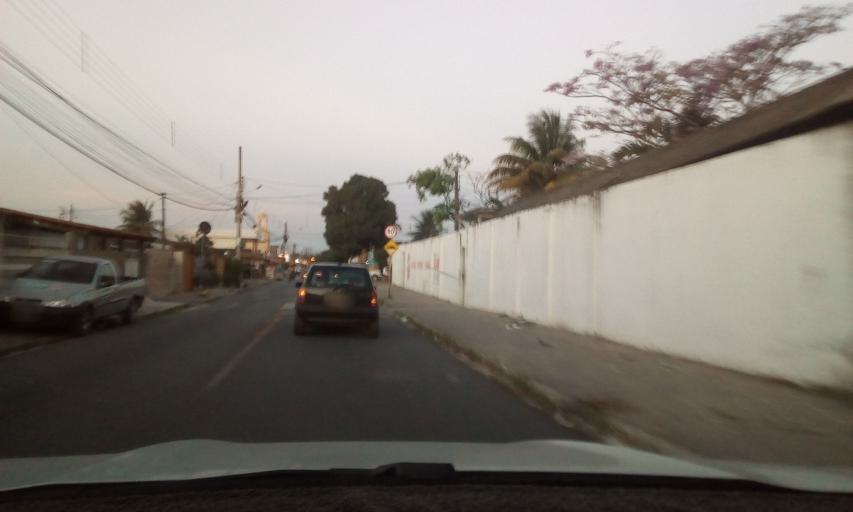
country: BR
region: Paraiba
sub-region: Bayeux
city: Bayeux
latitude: -7.1712
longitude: -34.9134
